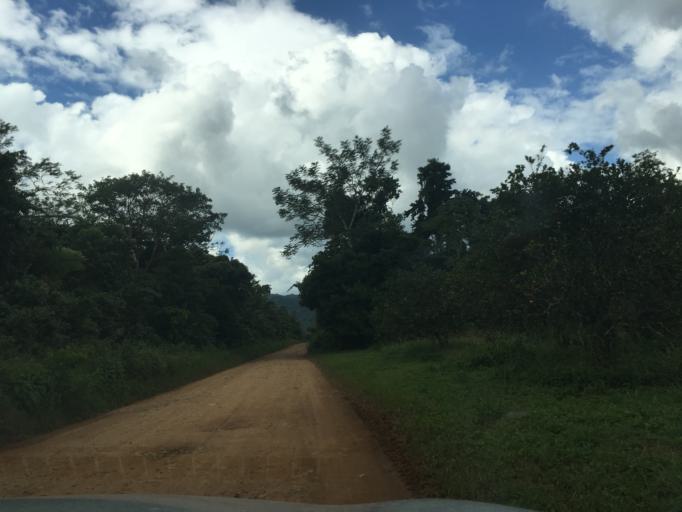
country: BZ
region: Stann Creek
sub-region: Dangriga
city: Dangriga
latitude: 16.9374
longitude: -88.3635
